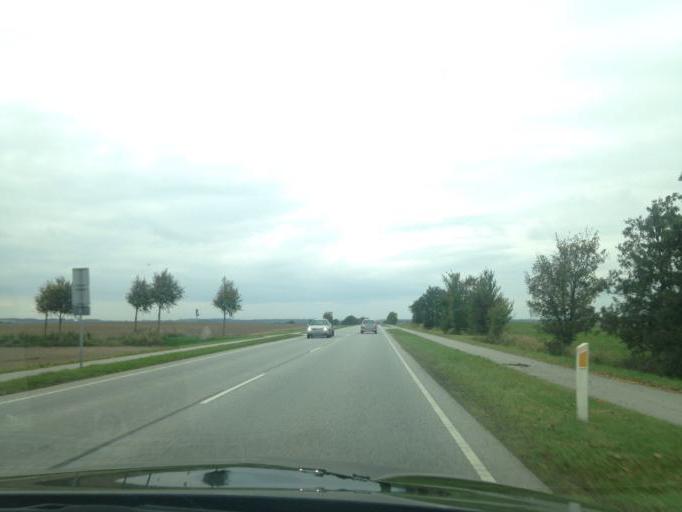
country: DK
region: South Denmark
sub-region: Kolding Kommune
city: Christiansfeld
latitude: 55.3284
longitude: 9.4927
